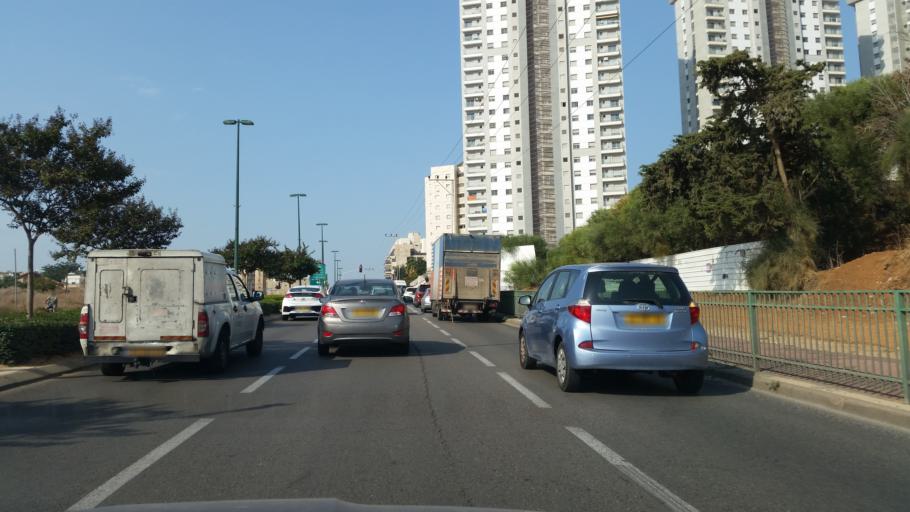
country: IL
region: Central District
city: Netanya
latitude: 32.3121
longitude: 34.8628
